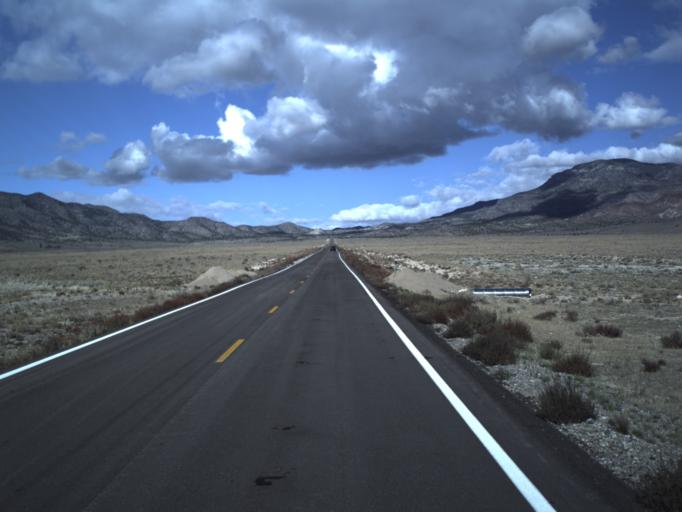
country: US
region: Utah
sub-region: Beaver County
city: Milford
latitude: 38.4859
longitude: -113.4543
